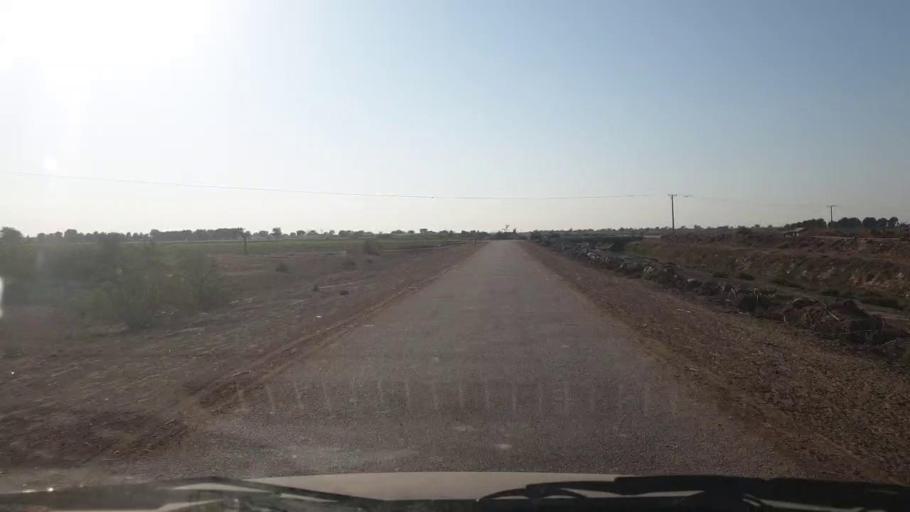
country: PK
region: Sindh
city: Samaro
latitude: 25.3518
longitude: 69.2939
